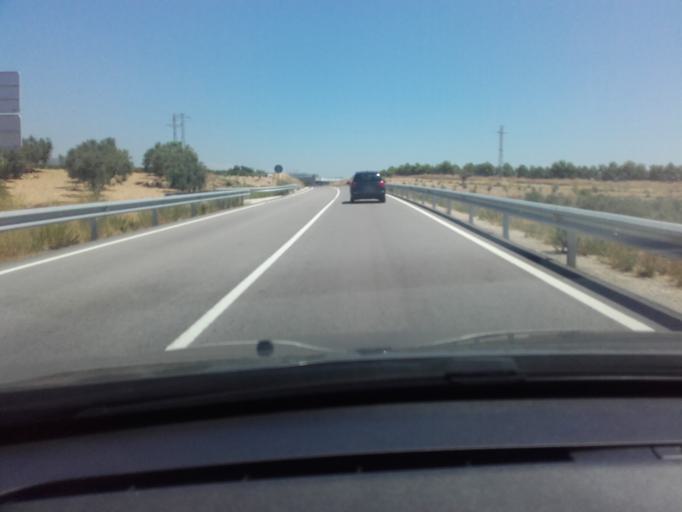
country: ES
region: Catalonia
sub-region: Provincia de Tarragona
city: Albinyana
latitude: 41.2663
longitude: 1.4992
